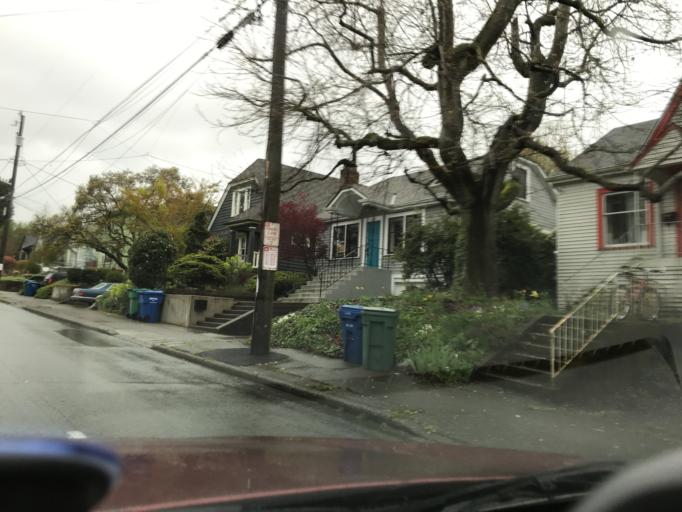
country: US
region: Washington
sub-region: King County
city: Seattle
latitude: 47.6739
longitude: -122.3007
